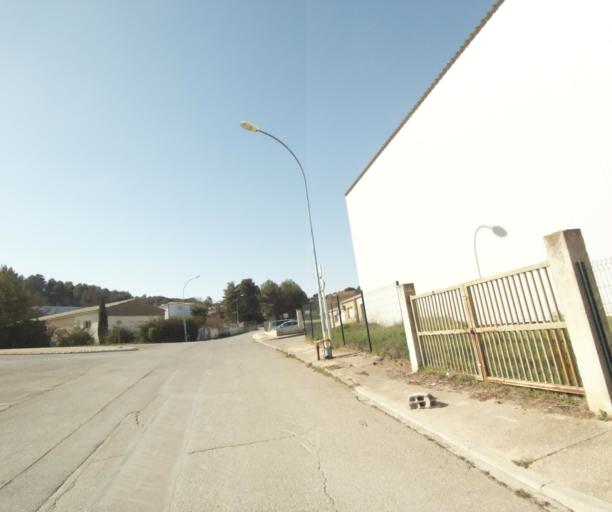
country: FR
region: Provence-Alpes-Cote d'Azur
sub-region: Departement des Bouches-du-Rhone
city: Gardanne
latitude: 43.4452
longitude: 5.4552
